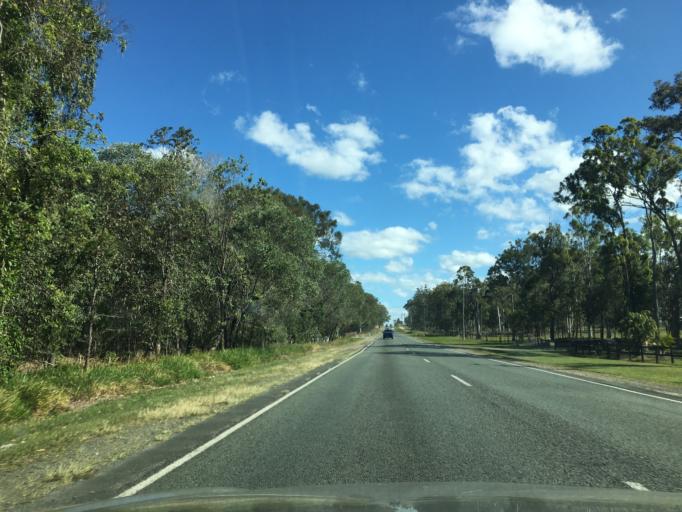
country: AU
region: Queensland
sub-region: Logan
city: Logan Reserve
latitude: -27.7356
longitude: 153.1283
